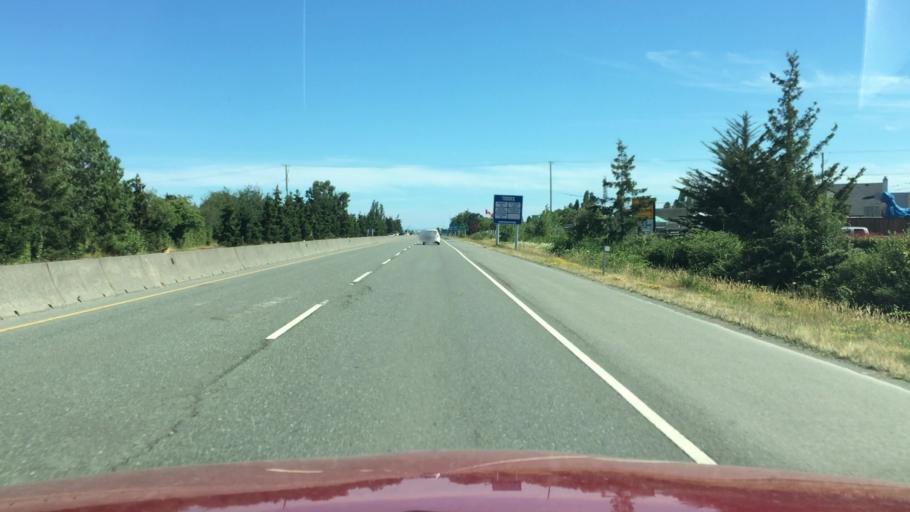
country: CA
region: British Columbia
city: North Saanich
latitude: 48.6568
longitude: -123.4128
